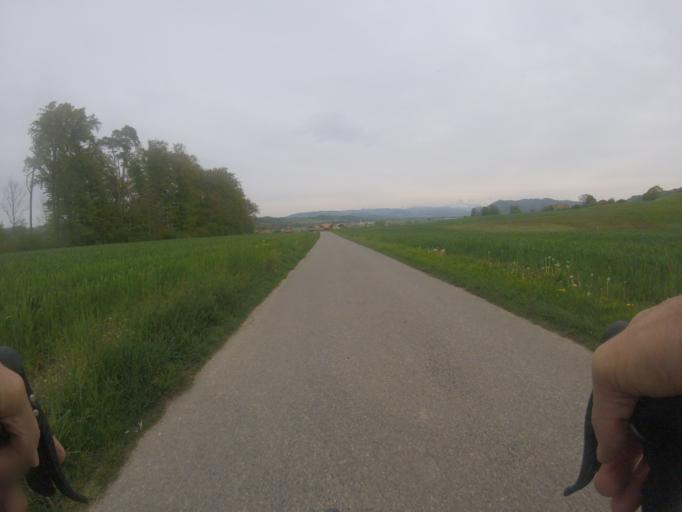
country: CH
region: Bern
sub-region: Bern-Mittelland District
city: Muri
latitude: 46.9174
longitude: 7.4869
